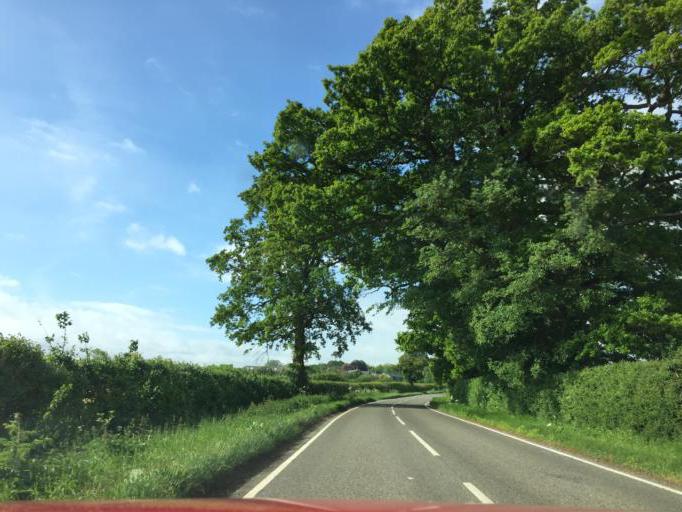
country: GB
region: England
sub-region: Northamptonshire
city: Towcester
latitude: 52.1288
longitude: -0.9598
